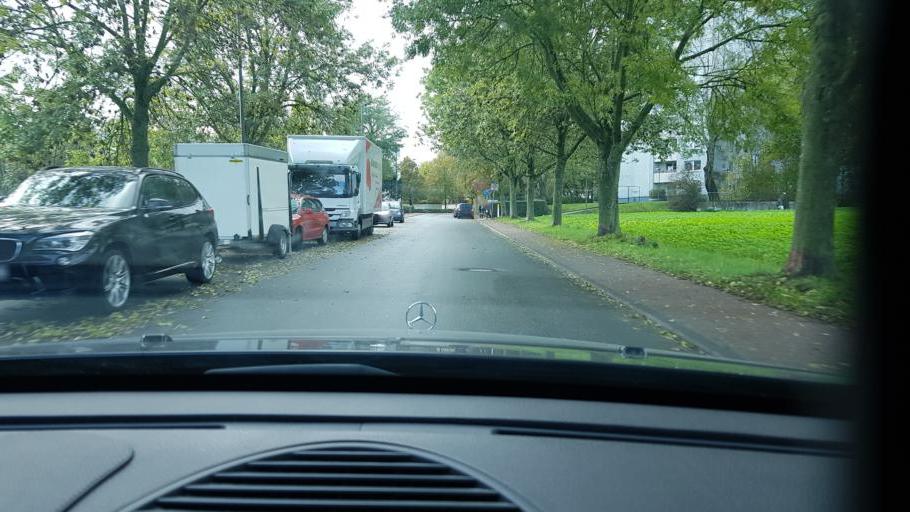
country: DE
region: Hesse
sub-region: Regierungsbezirk Darmstadt
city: Steinbach am Taunus
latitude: 50.1662
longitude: 8.5869
